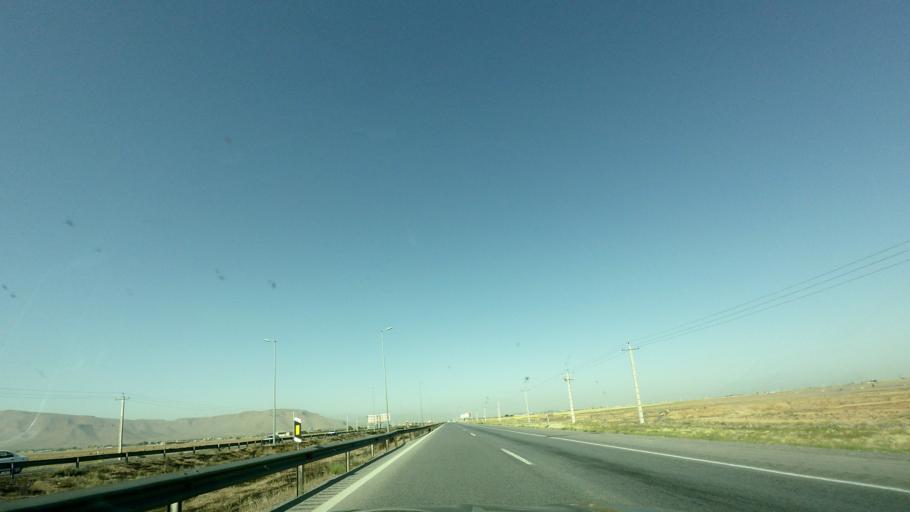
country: IR
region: Markazi
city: Arak
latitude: 34.1632
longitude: 50.0219
